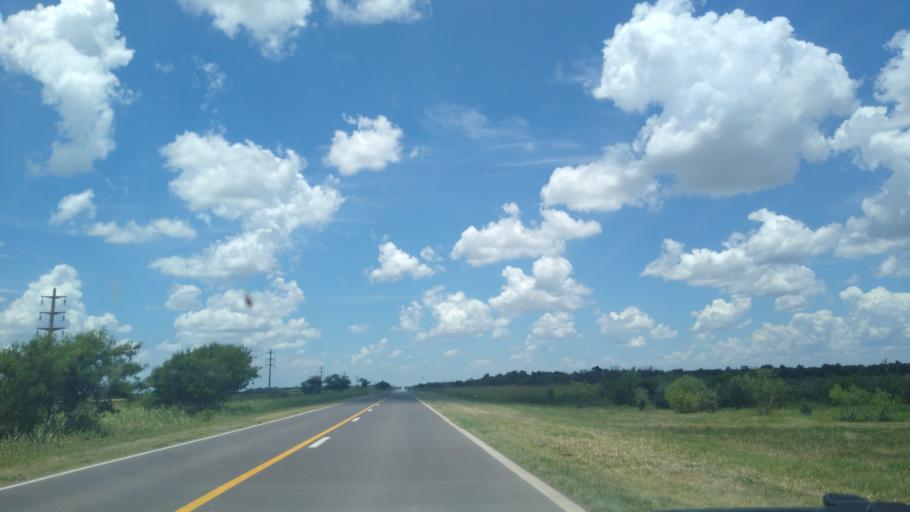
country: AR
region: Chaco
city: Presidencia Roque Saenz Pena
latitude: -26.7369
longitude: -60.3852
